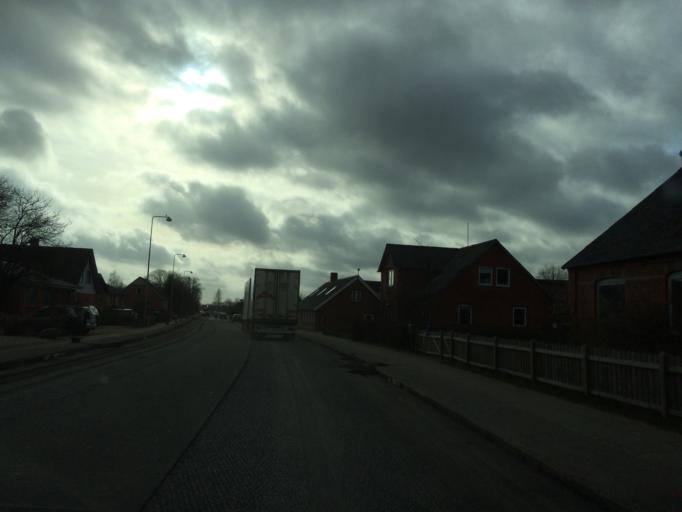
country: DK
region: Central Jutland
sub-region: Viborg Kommune
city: Bjerringbro
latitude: 56.4956
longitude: 9.7039
